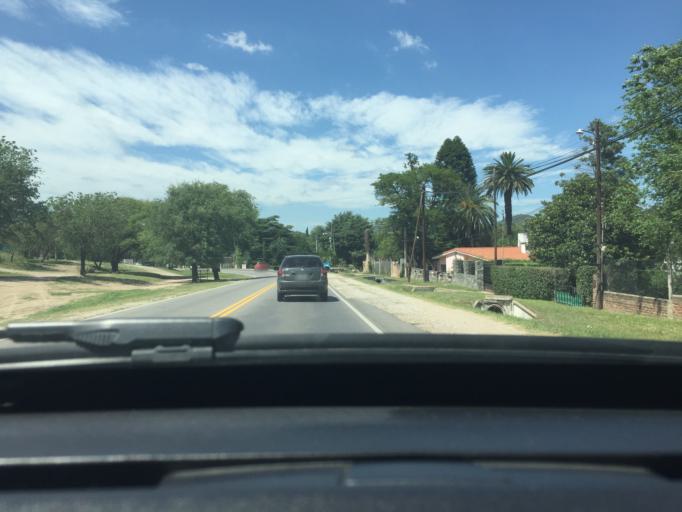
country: AR
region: Cordoba
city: Alta Gracia
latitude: -31.7331
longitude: -64.4323
